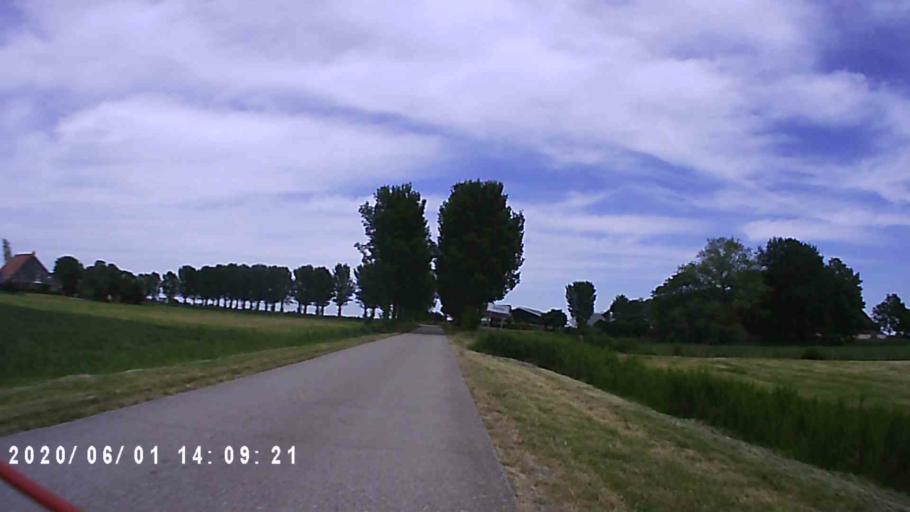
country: NL
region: Friesland
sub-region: Gemeente Littenseradiel
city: Winsum
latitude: 53.1225
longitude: 5.6455
